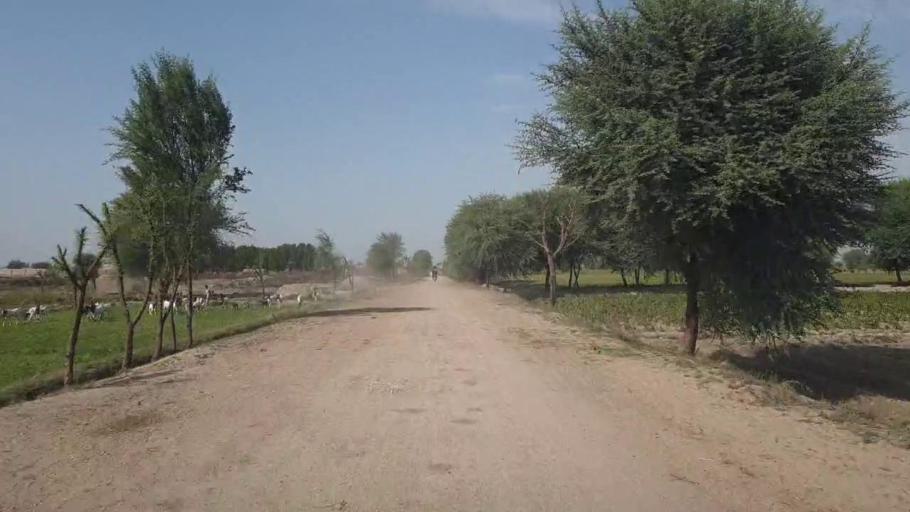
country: PK
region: Sindh
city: Dhoro Naro
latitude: 25.4427
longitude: 69.5490
